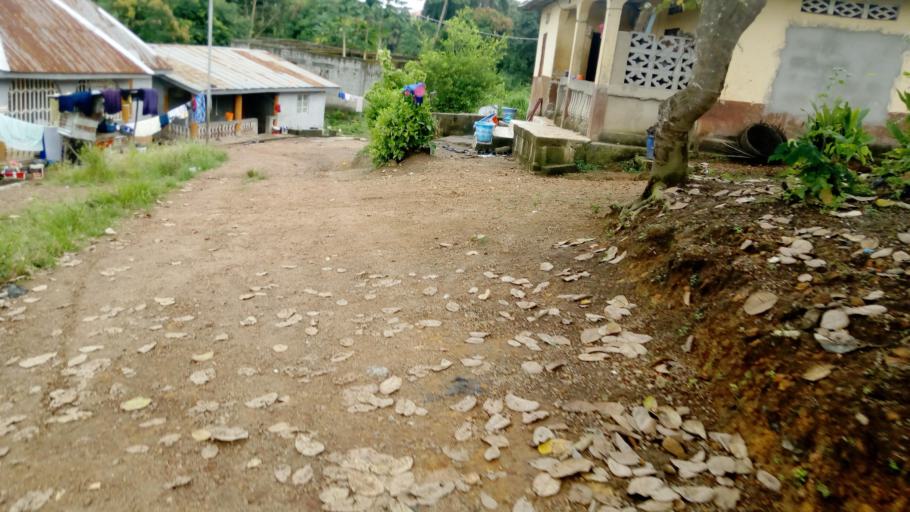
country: SL
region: Northern Province
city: Makeni
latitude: 8.8905
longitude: -12.0301
